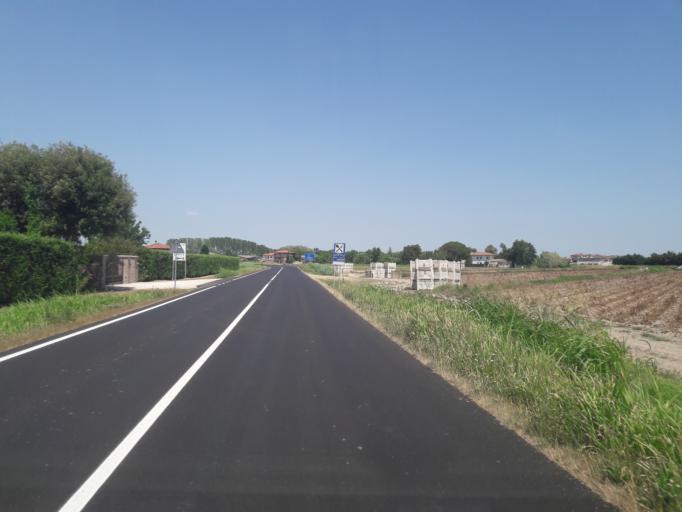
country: IT
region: Veneto
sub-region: Provincia di Rovigo
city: Taglio di Po
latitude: 45.0012
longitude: 12.2024
